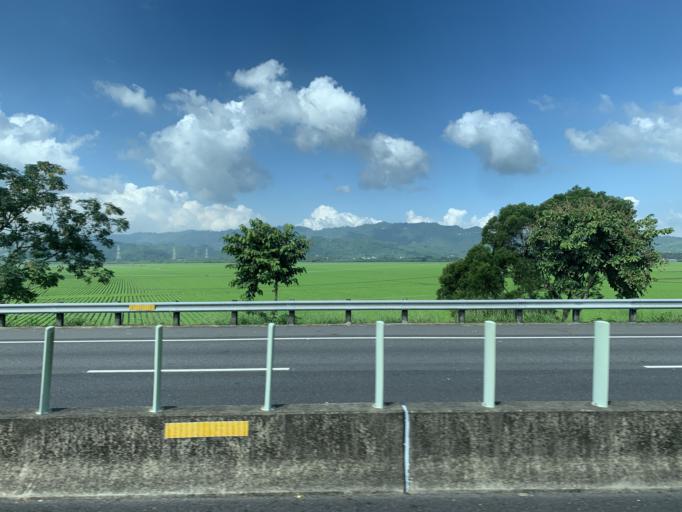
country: TW
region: Taiwan
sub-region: Pingtung
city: Pingtung
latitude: 22.8238
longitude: 120.4877
